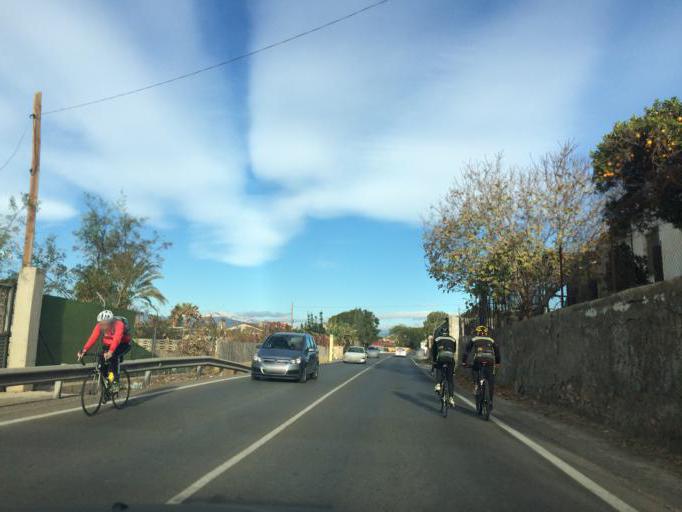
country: ES
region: Andalusia
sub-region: Provincia de Almeria
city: Viator
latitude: 36.8992
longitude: -2.4331
